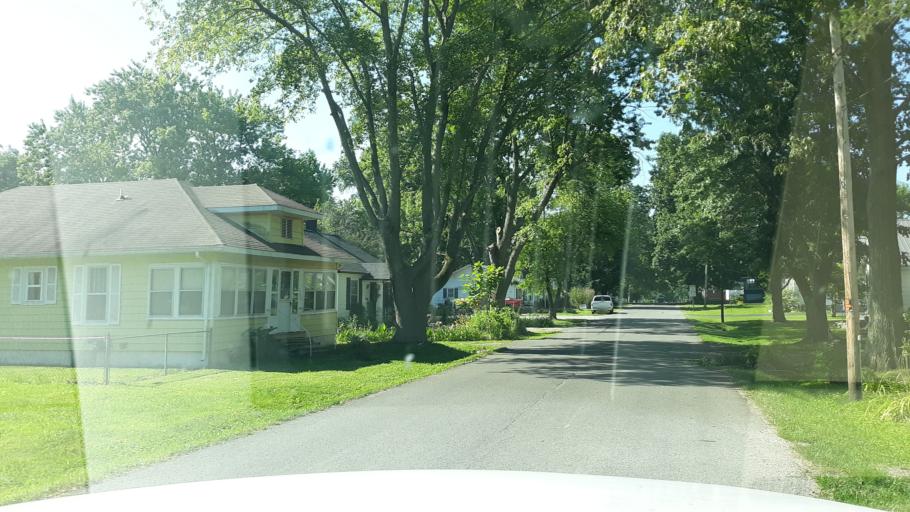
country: US
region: Illinois
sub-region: Saline County
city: Eldorado
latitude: 37.8228
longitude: -88.4350
